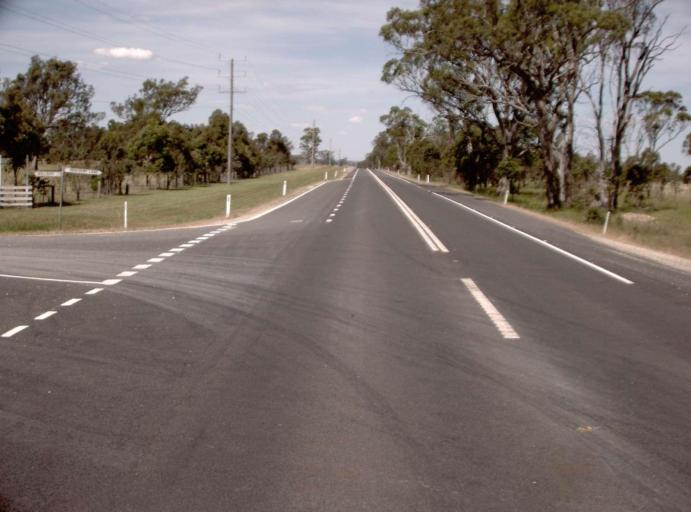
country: AU
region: Victoria
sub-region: East Gippsland
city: Bairnsdale
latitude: -37.8657
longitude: 147.4921
